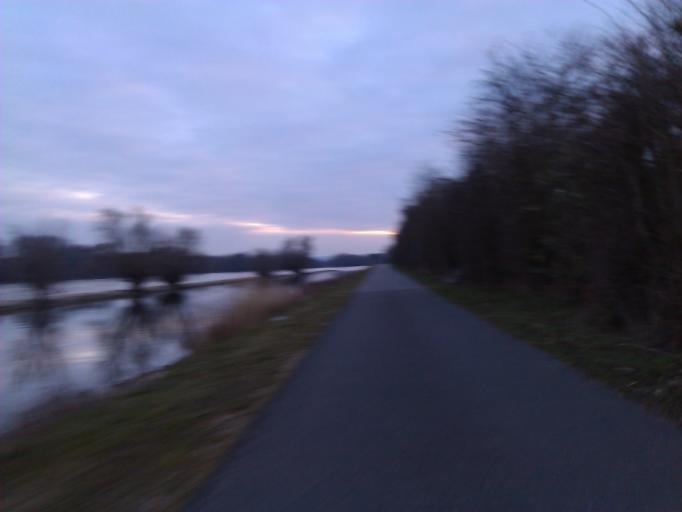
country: DE
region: Hesse
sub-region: Regierungsbezirk Darmstadt
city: Kiedrich
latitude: 50.0141
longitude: 8.0737
